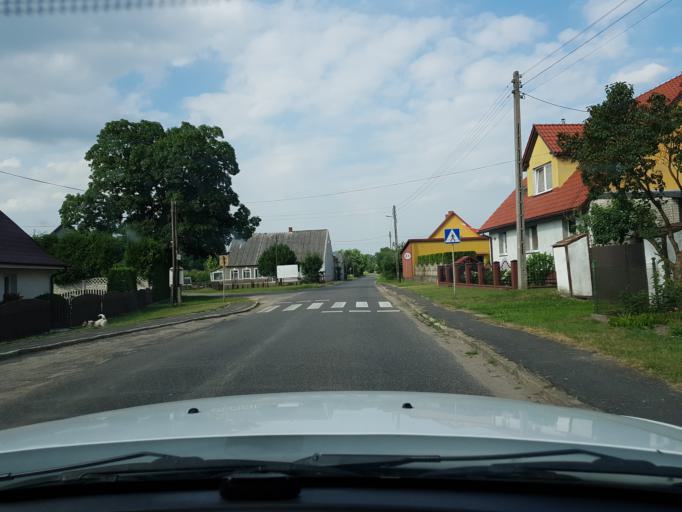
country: PL
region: West Pomeranian Voivodeship
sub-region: Powiat gryfinski
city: Chojna
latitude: 52.9926
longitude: 14.4863
